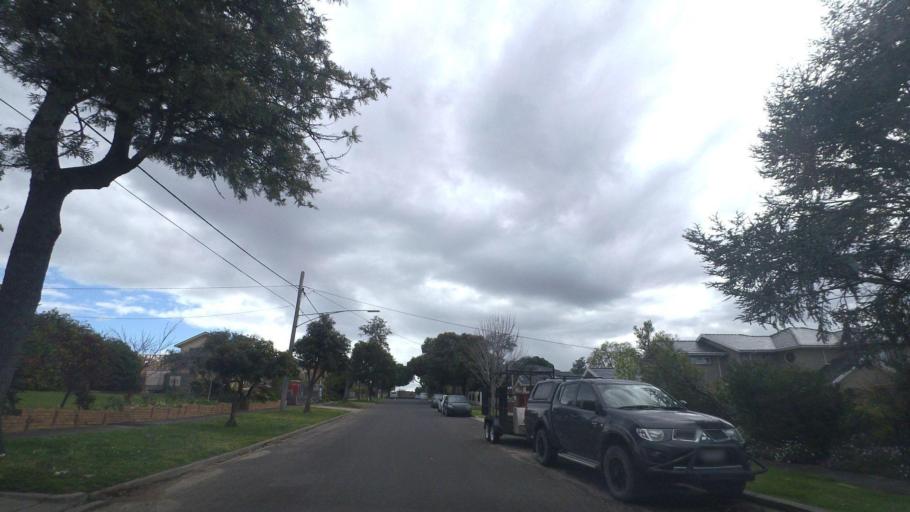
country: AU
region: Victoria
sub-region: Banyule
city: Heidelberg Heights
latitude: -37.7422
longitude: 145.0598
